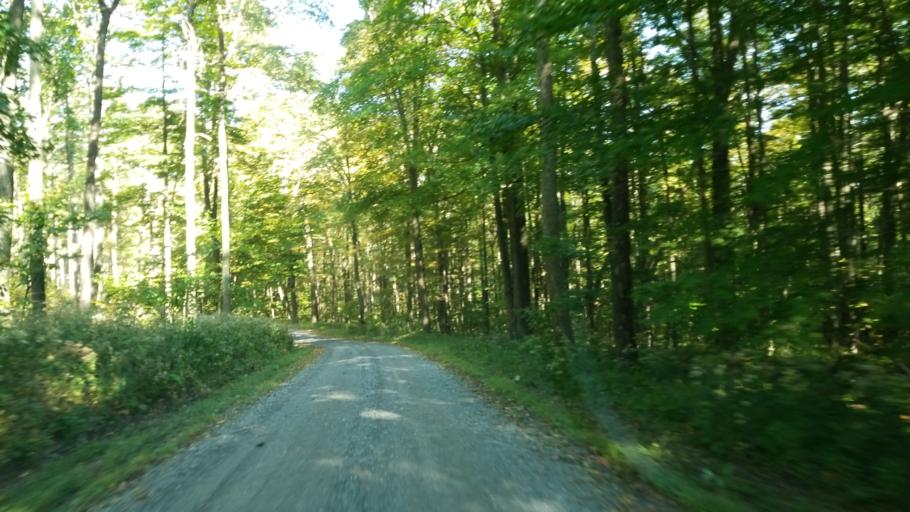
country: US
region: Pennsylvania
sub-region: Clearfield County
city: Treasure Lake
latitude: 41.1407
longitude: -78.5732
